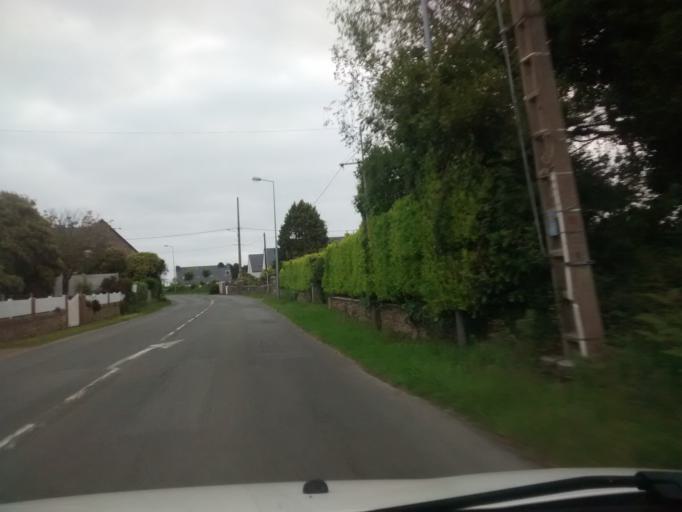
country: FR
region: Brittany
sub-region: Departement des Cotes-d'Armor
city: Tregastel
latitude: 48.8098
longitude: -3.4750
